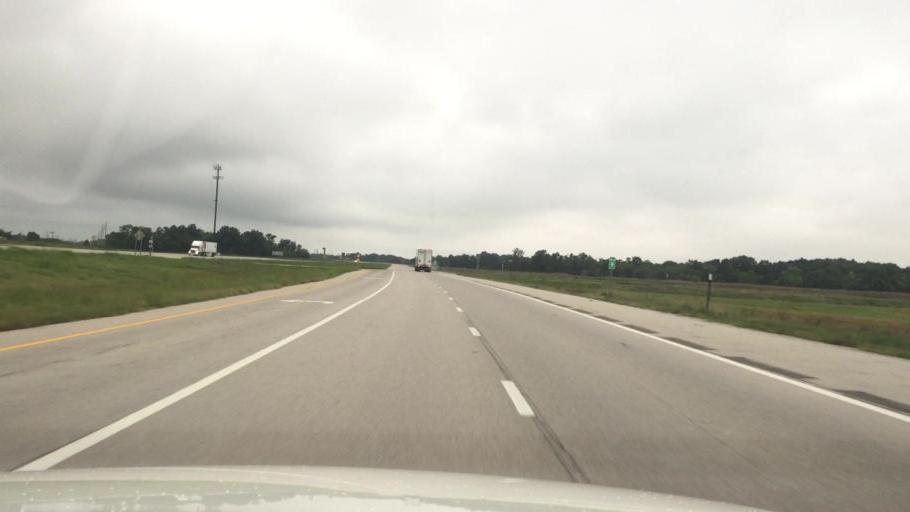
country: US
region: Kansas
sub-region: Montgomery County
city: Coffeyville
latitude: 37.1096
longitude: -95.5862
